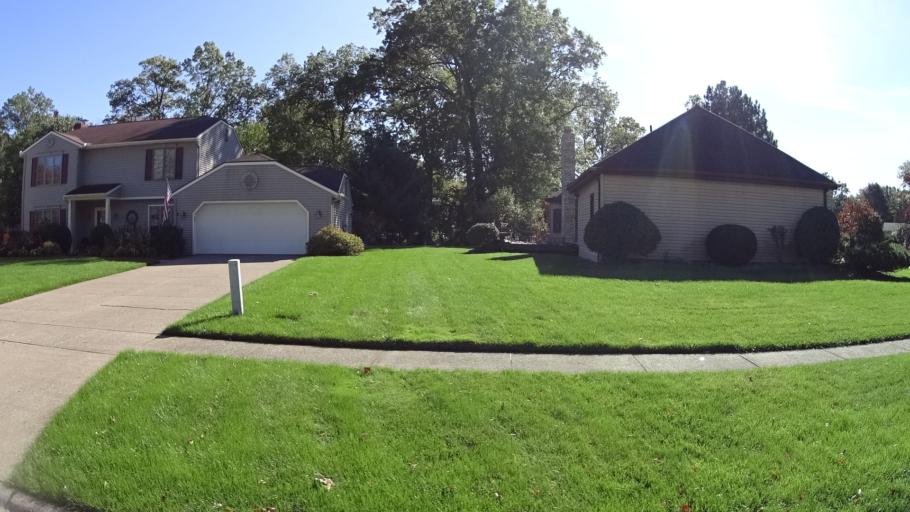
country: US
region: Ohio
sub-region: Lorain County
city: Lorain
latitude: 41.4197
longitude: -82.1744
